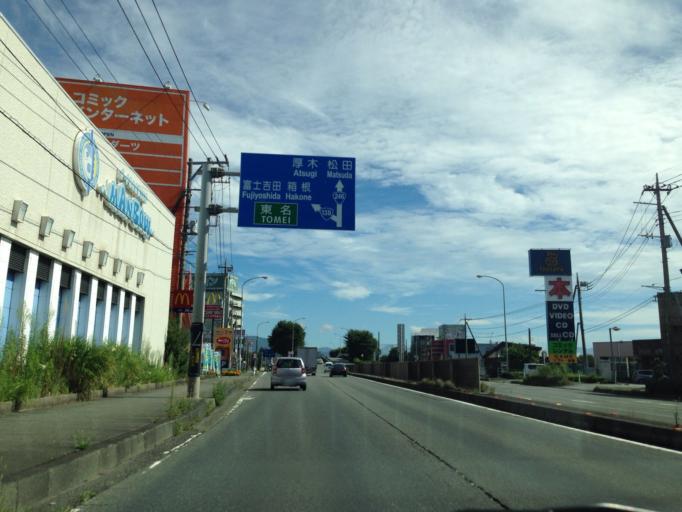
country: JP
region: Shizuoka
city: Gotemba
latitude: 35.3101
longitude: 138.9263
